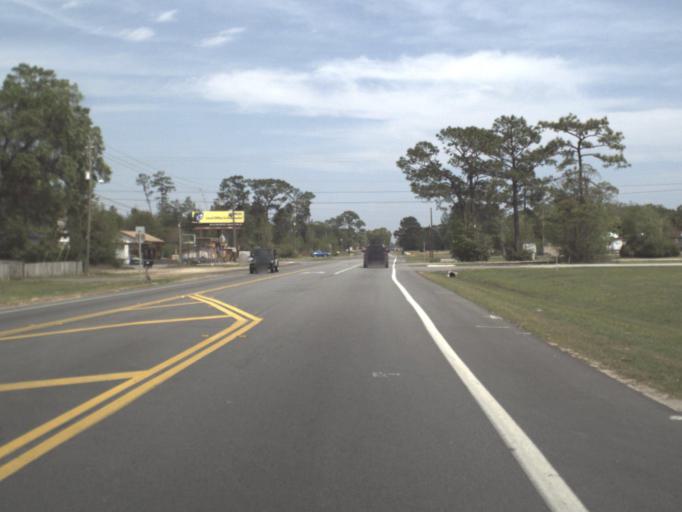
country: US
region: Florida
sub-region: Escambia County
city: Ensley
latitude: 30.5344
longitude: -87.3277
